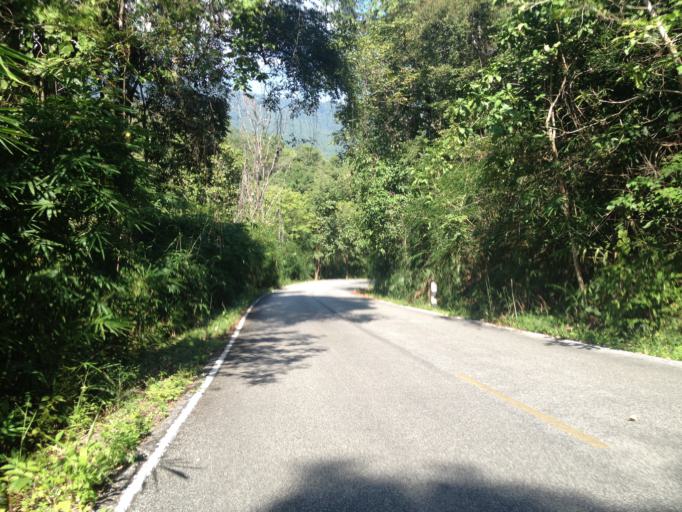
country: TH
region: Chiang Mai
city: Hang Dong
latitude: 18.7525
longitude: 98.8984
